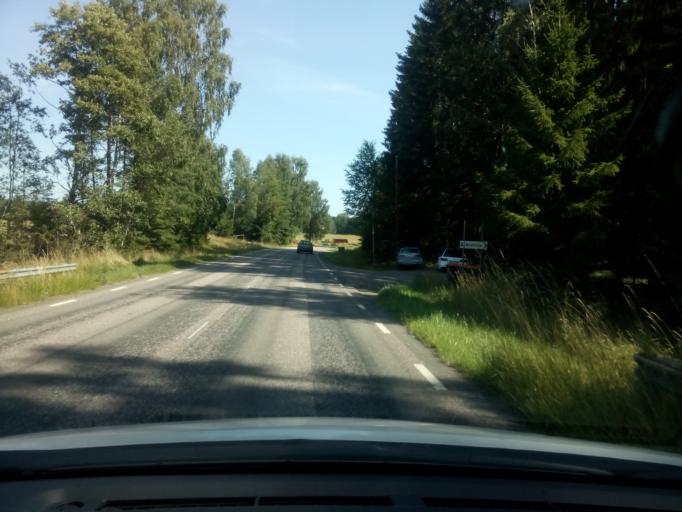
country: SE
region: Soedermanland
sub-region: Oxelosunds Kommun
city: Oxelosund
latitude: 58.7577
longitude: 17.2915
